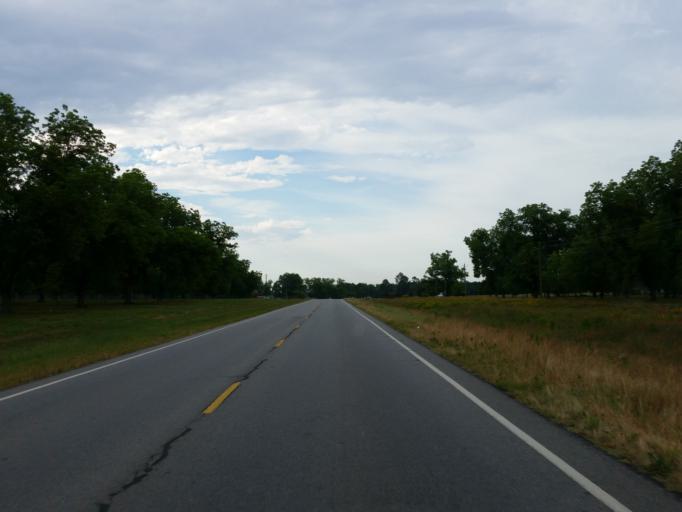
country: US
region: Georgia
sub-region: Dooly County
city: Vienna
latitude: 32.0437
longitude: -83.7953
